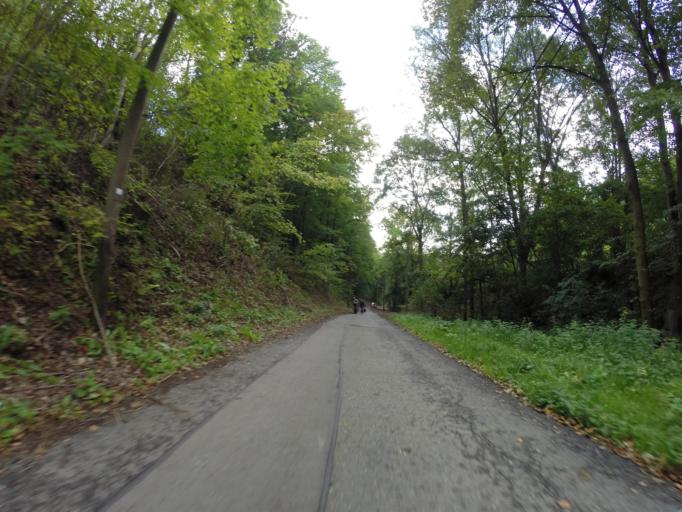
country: DE
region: Thuringia
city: Jena
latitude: 50.9428
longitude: 11.5667
